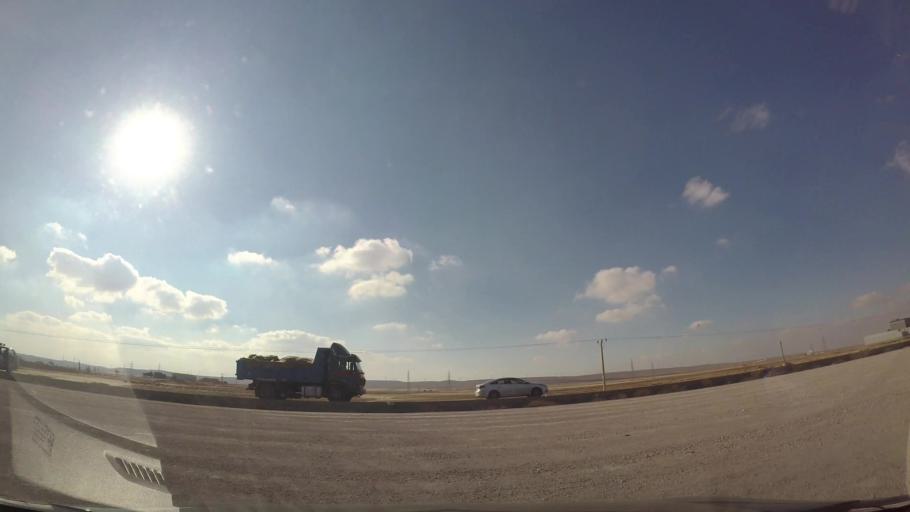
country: JO
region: Karak
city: Adir
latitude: 31.2767
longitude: 36.0540
